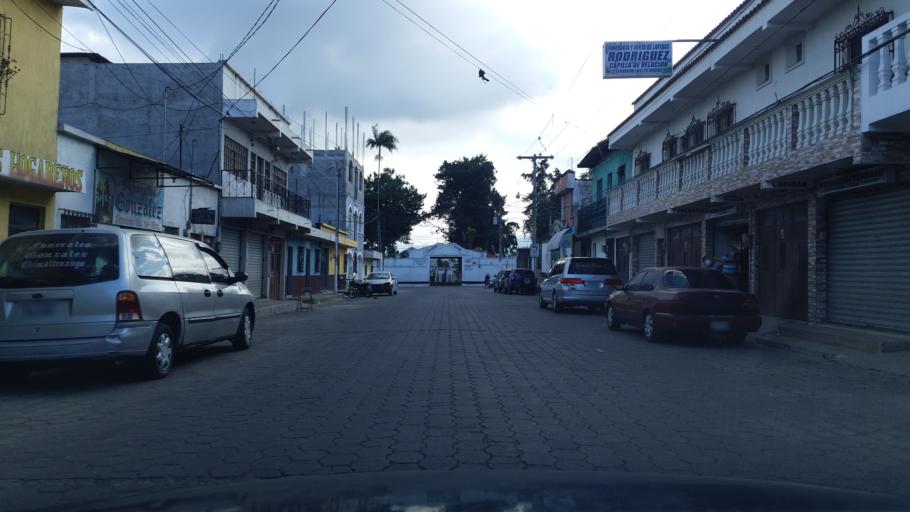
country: GT
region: Chimaltenango
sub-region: Municipio de Chimaltenango
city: Chimaltenango
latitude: 14.6573
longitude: -90.8157
